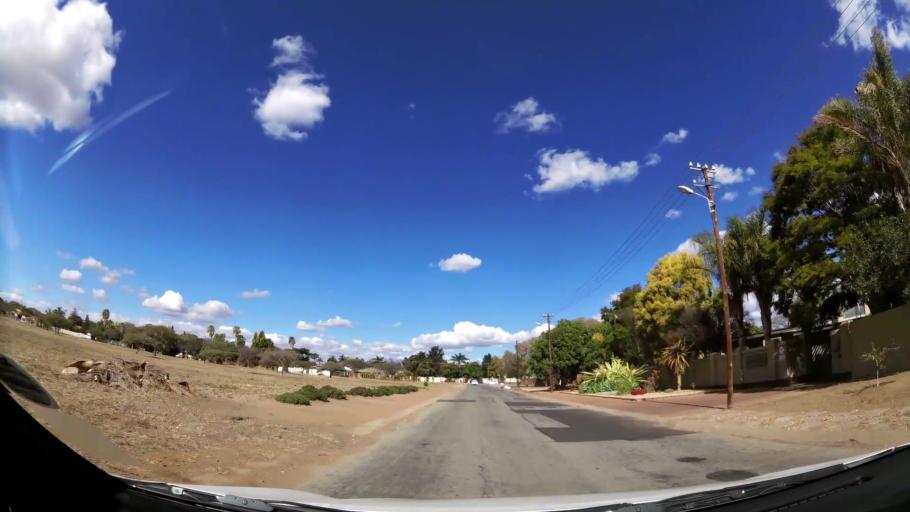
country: ZA
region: Limpopo
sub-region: Capricorn District Municipality
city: Polokwane
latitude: -23.8861
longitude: 29.4640
